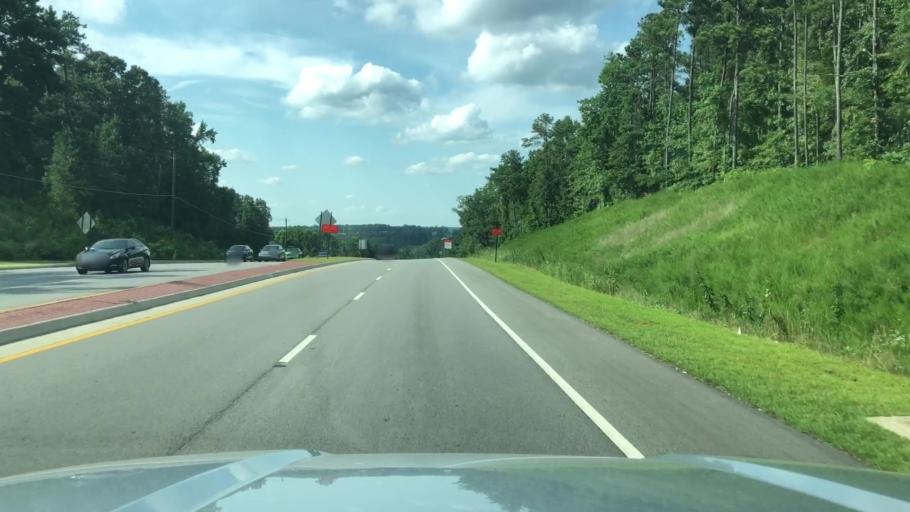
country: US
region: Georgia
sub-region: Paulding County
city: Hiram
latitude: 33.8699
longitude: -84.7810
